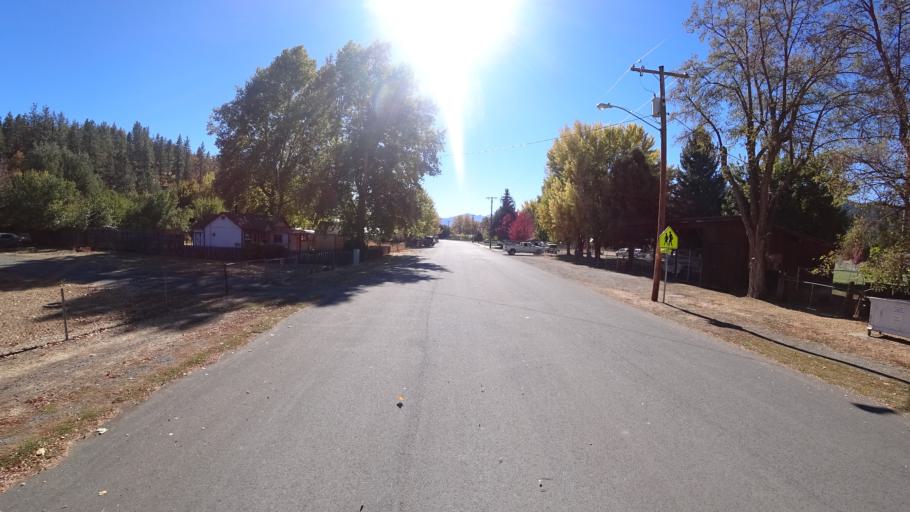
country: US
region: California
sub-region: Siskiyou County
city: Yreka
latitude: 41.6051
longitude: -122.8446
